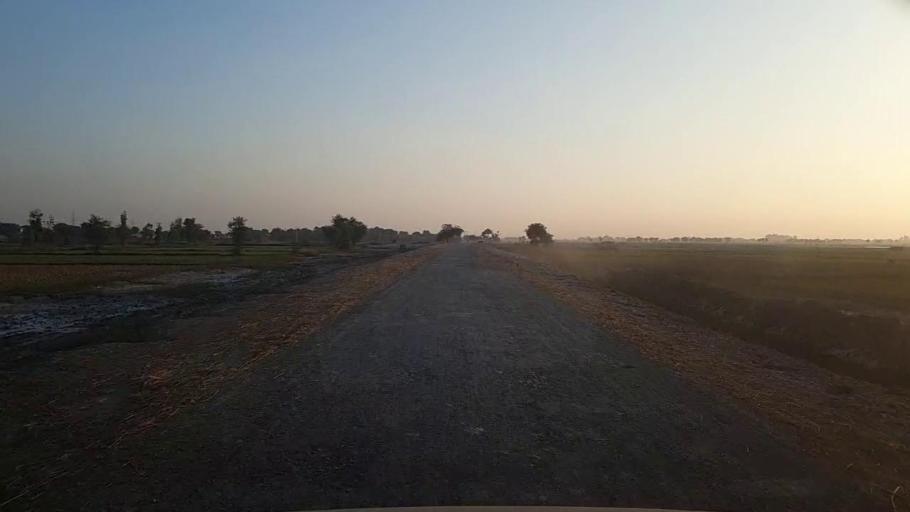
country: PK
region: Sindh
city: Khairpur Nathan Shah
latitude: 27.1758
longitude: 67.7340
